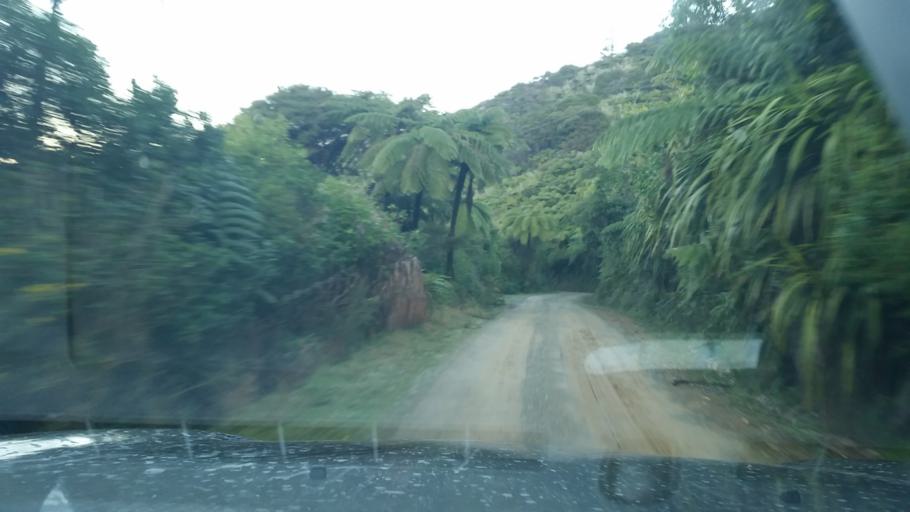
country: NZ
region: Marlborough
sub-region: Marlborough District
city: Picton
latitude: -41.1305
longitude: 174.1437
